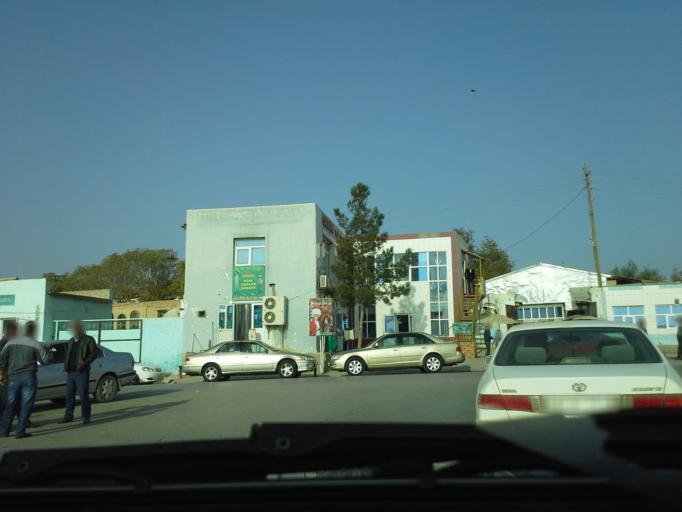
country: TM
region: Lebap
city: Atamyrat
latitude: 37.8508
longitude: 65.2388
